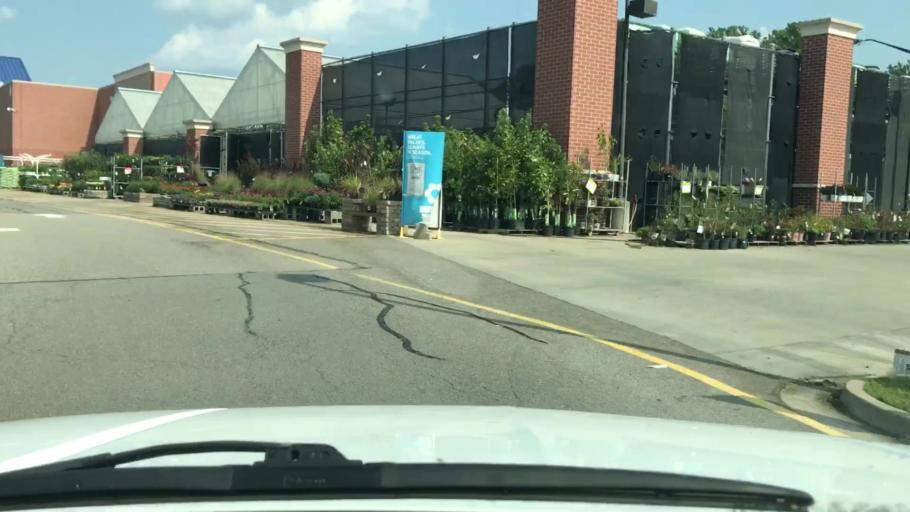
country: US
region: Virginia
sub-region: Hanover County
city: Mechanicsville
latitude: 37.6129
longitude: -77.3275
